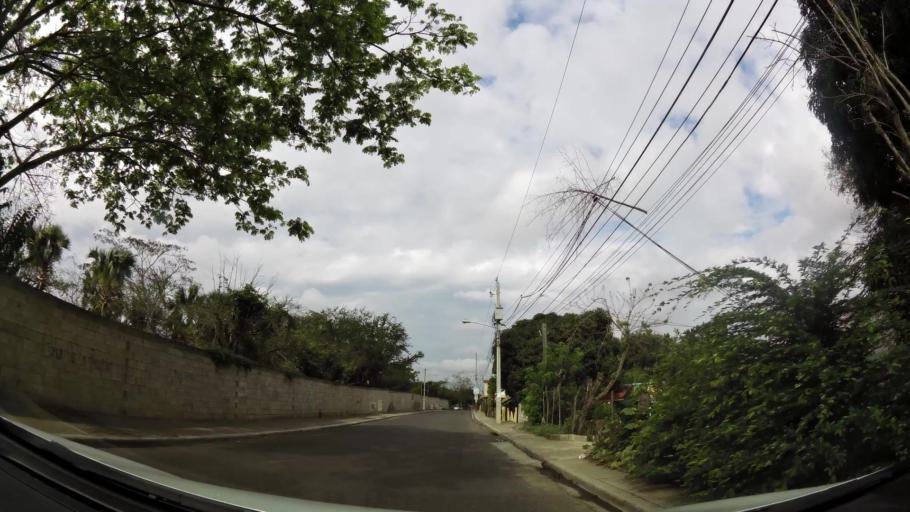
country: DO
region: Santiago
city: Santiago de los Caballeros
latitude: 19.4264
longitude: -70.6651
